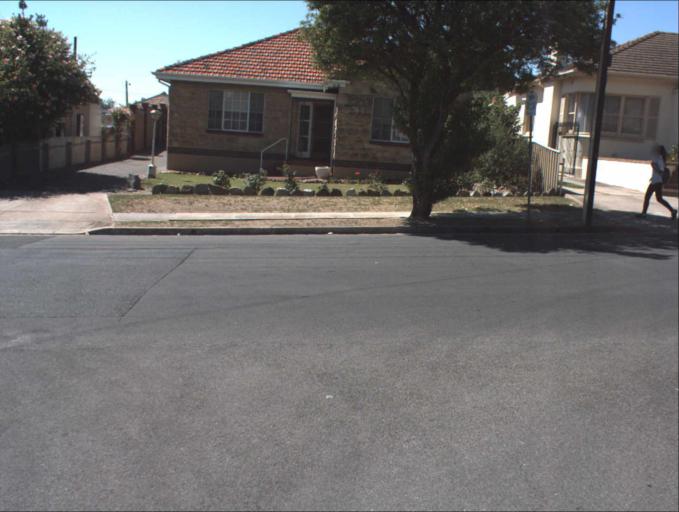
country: AU
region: South Australia
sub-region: Port Adelaide Enfield
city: Blair Athol
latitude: -34.8608
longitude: 138.6023
